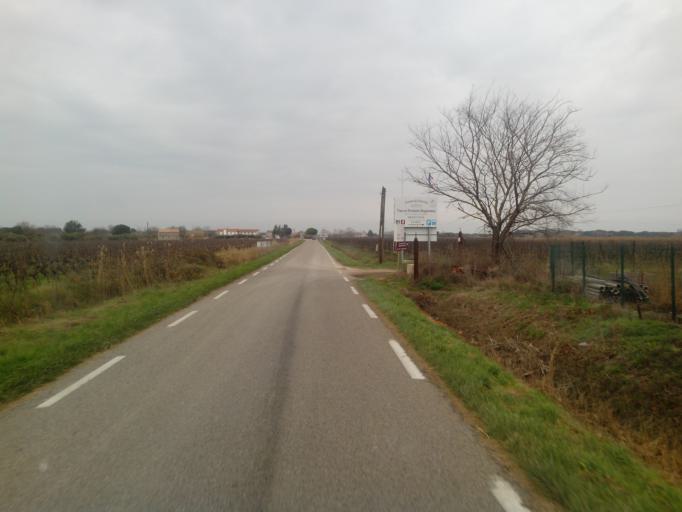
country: FR
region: Languedoc-Roussillon
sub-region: Departement du Gard
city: Aigues-Mortes
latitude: 43.5713
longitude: 4.3129
